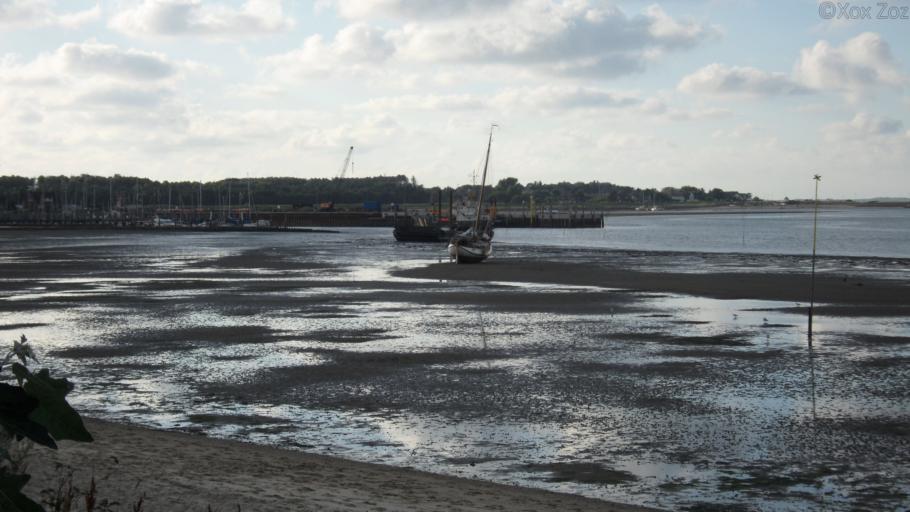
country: DE
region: Schleswig-Holstein
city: Hooge
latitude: 54.5788
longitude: 8.5562
